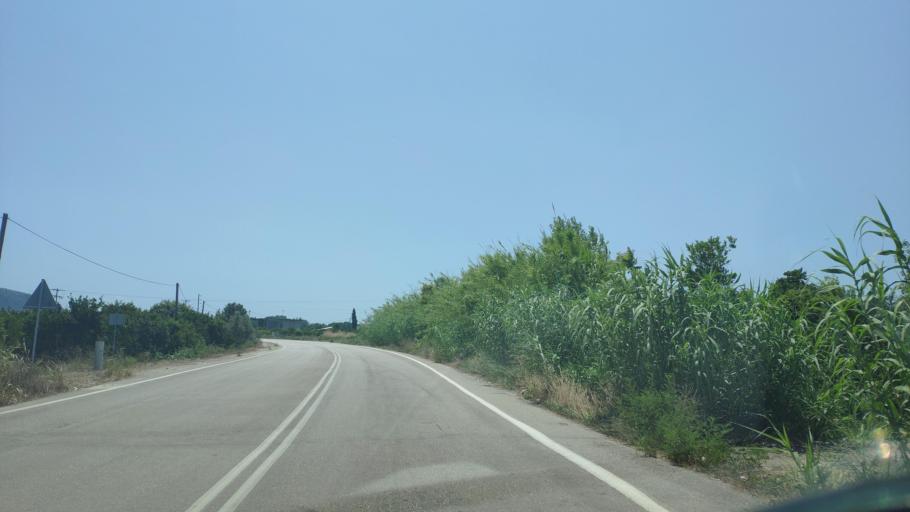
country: GR
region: Epirus
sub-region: Nomos Artas
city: Kostakioi
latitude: 39.1276
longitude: 20.9845
